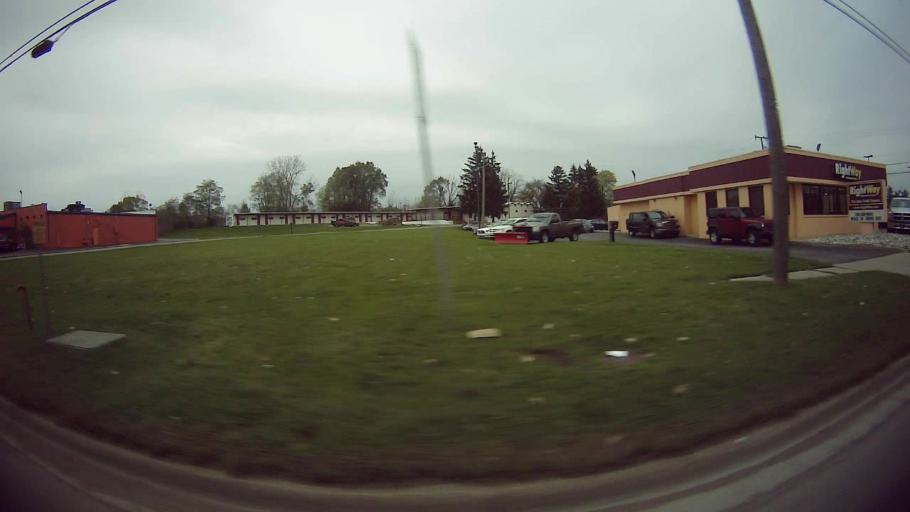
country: US
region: Michigan
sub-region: Oakland County
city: Pontiac
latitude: 42.6657
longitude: -83.3308
